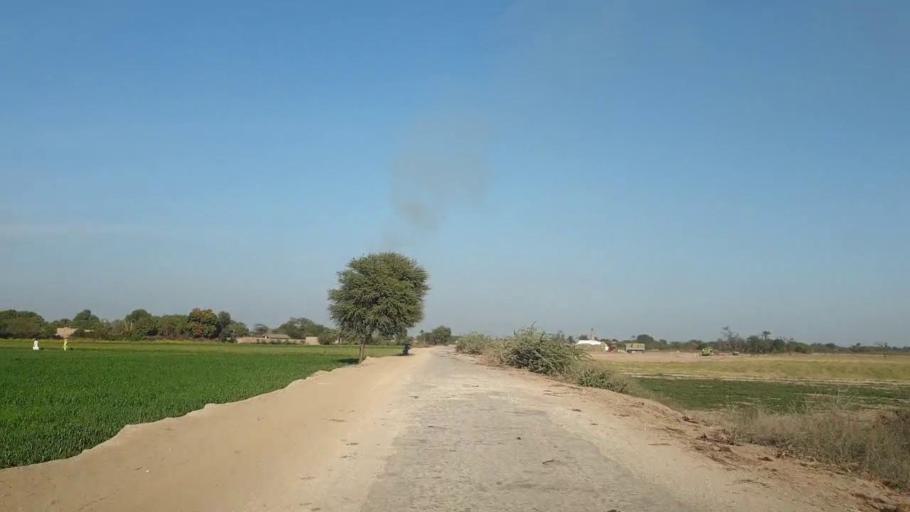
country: PK
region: Sindh
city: Tando Adam
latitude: 25.6993
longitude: 68.6900
